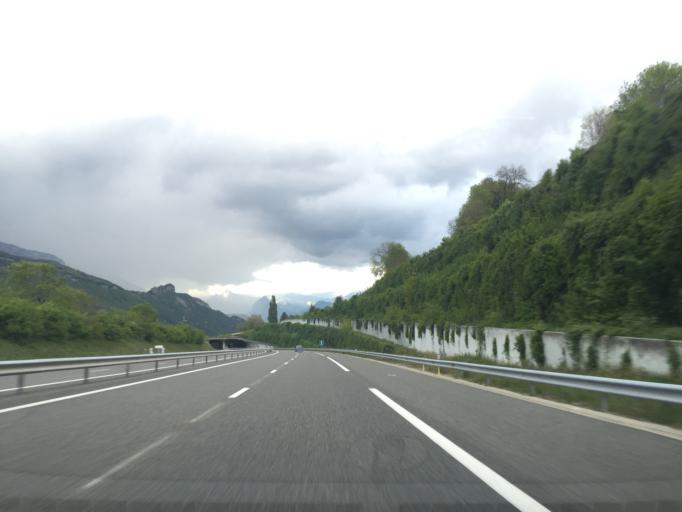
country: FR
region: Rhone-Alpes
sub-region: Departement de l'Isere
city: Vif
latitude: 45.0235
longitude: 5.6620
